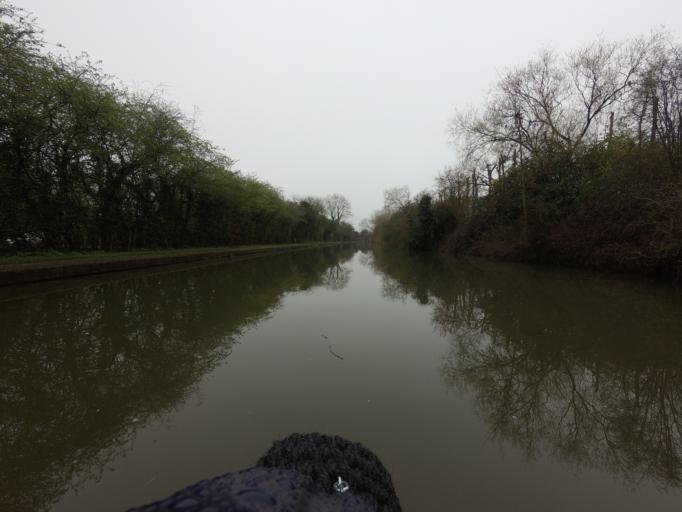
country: GB
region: England
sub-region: Milton Keynes
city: Simpson
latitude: 52.0111
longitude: -0.7160
